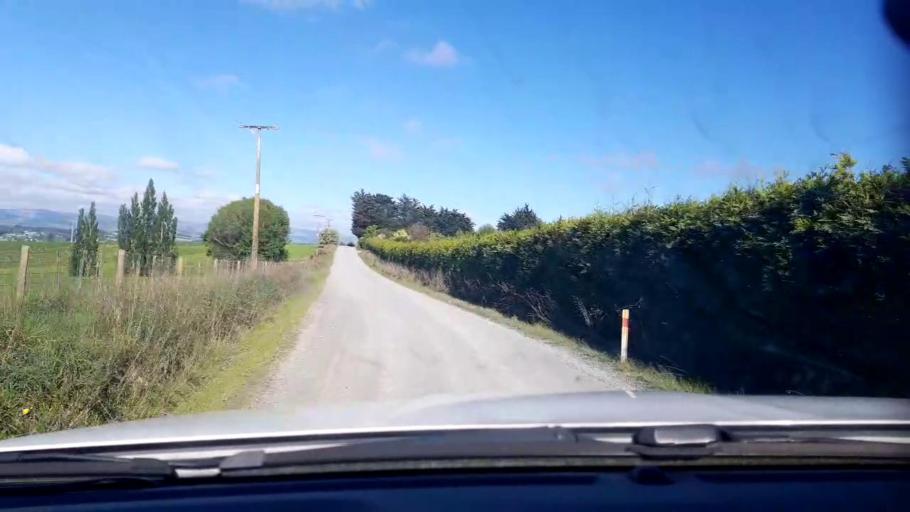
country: NZ
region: Otago
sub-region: Clutha District
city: Balclutha
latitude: -46.2232
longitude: 169.7616
